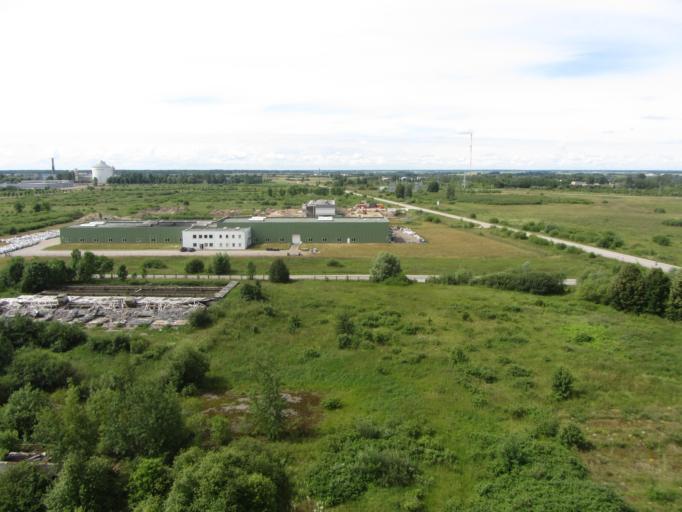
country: LT
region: Kauno apskritis
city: Kedainiai
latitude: 55.2705
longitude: 24.0034
